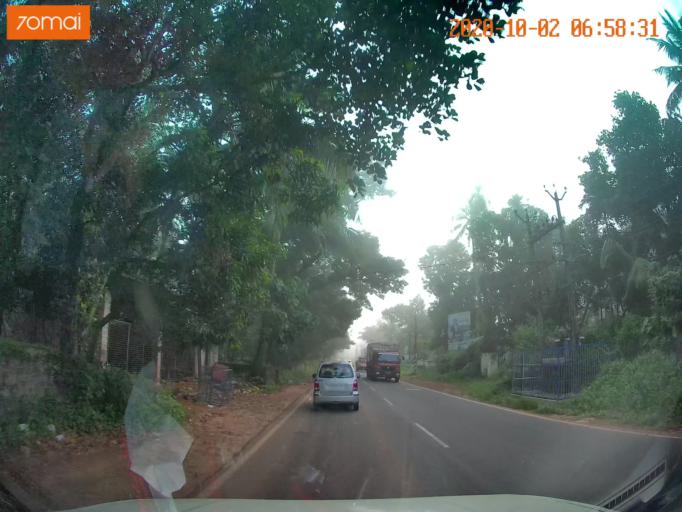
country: IN
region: Kerala
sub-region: Malappuram
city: Tirur
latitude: 10.8731
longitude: 76.0596
